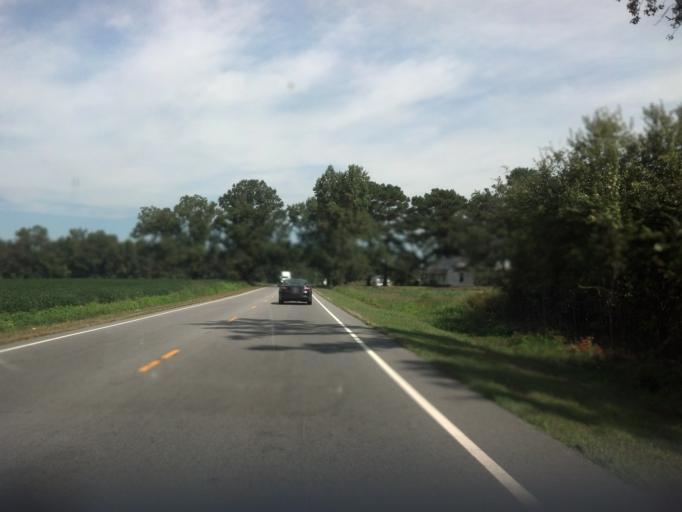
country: US
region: North Carolina
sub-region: Greene County
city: Maury
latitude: 35.5192
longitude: -77.6145
